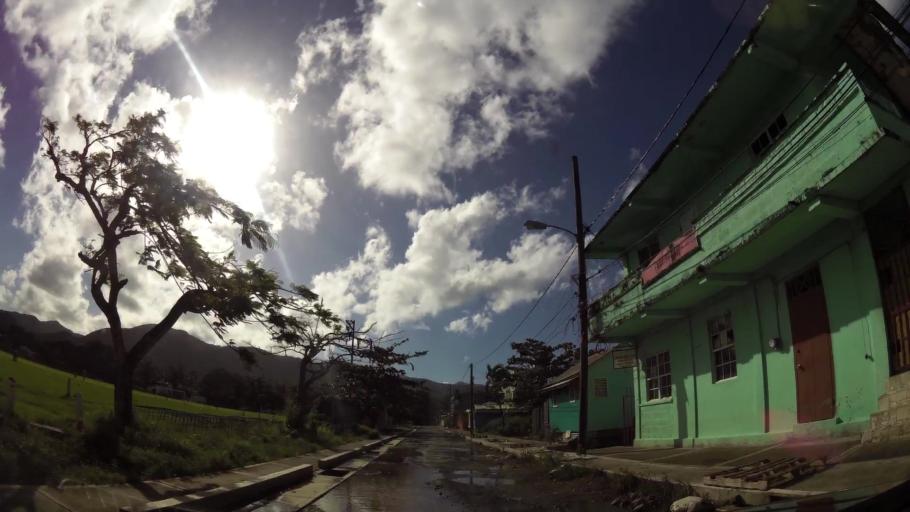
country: DM
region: Saint John
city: Portsmouth
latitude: 15.5754
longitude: -61.4556
